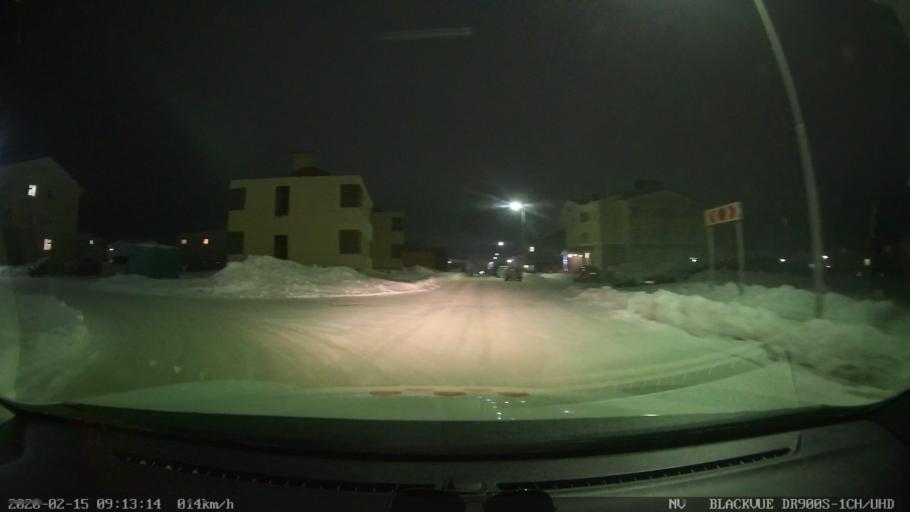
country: RU
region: Tatarstan
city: Stolbishchi
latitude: 55.7052
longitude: 49.3595
